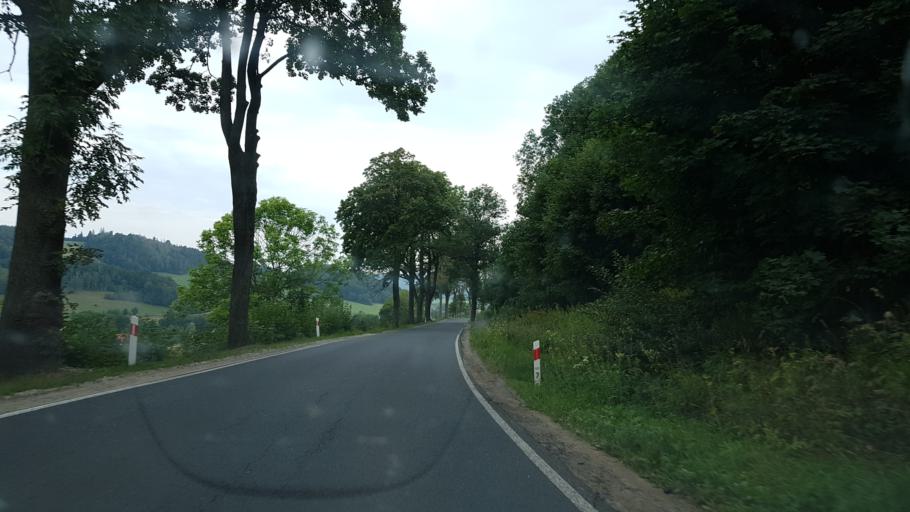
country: PL
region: Lower Silesian Voivodeship
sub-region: Powiat kamiennogorski
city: Marciszow
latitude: 50.8930
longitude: 15.9909
